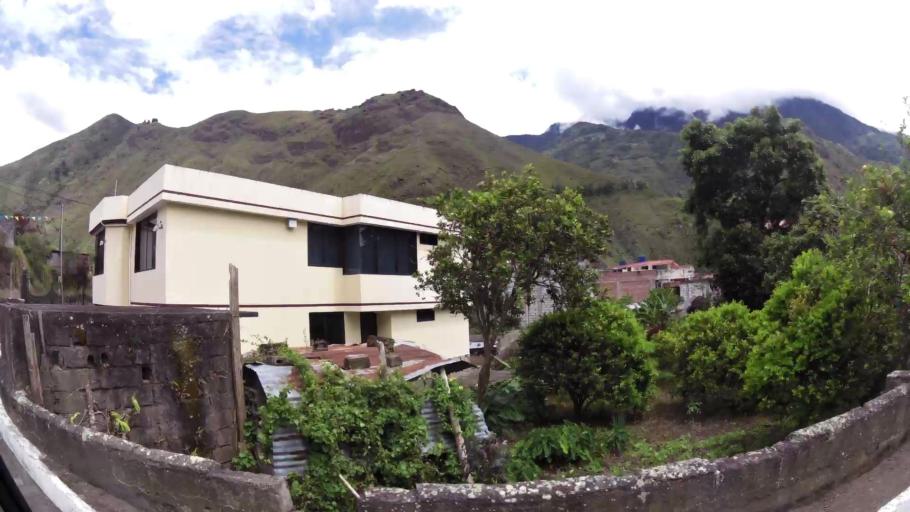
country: EC
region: Tungurahua
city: Banos
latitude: -1.3952
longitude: -78.3971
